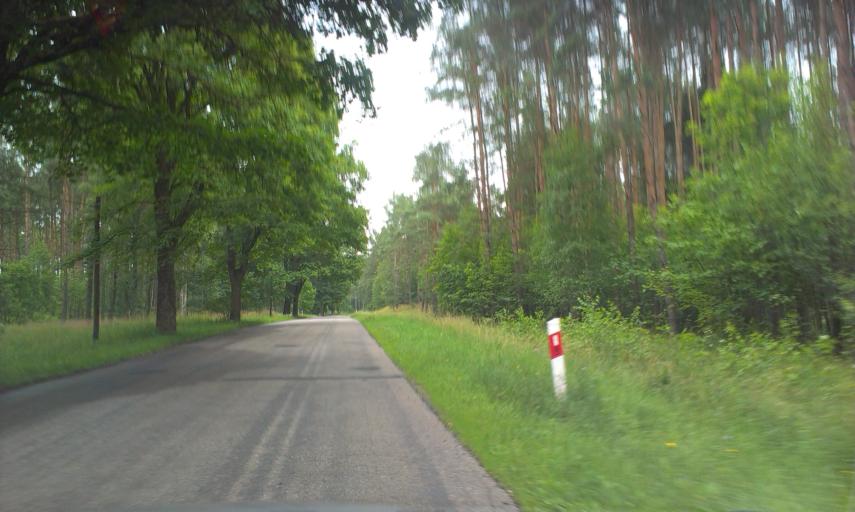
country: PL
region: West Pomeranian Voivodeship
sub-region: Powiat szczecinecki
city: Barwice
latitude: 53.6581
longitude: 16.3269
